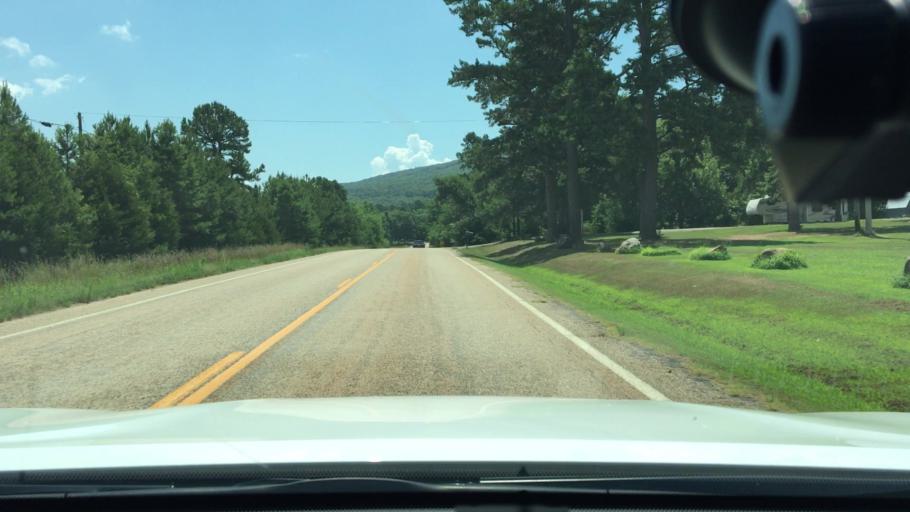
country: US
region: Arkansas
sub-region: Logan County
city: Paris
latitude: 35.1920
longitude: -93.6265
